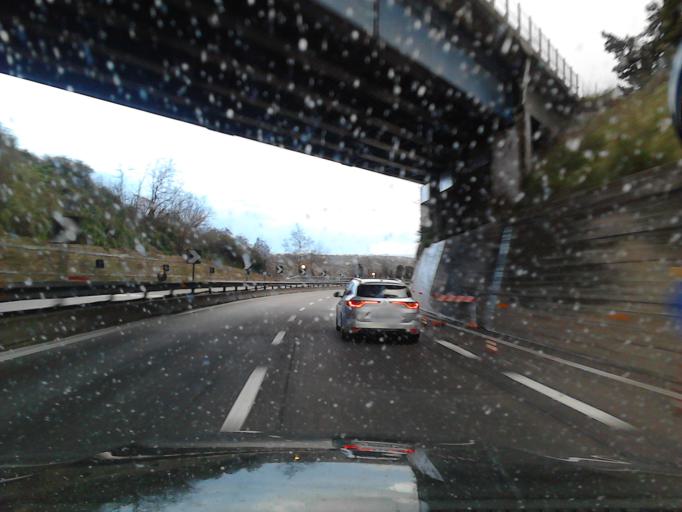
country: IT
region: Abruzzo
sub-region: Provincia di Chieti
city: Treglio
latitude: 42.2701
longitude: 14.4342
